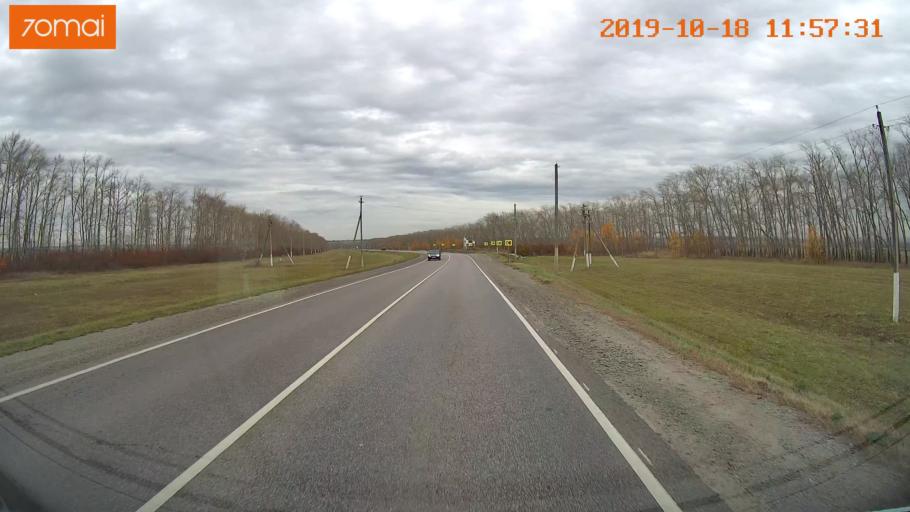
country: RU
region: Rjazan
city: Mikhaylov
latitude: 54.2665
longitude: 39.1458
